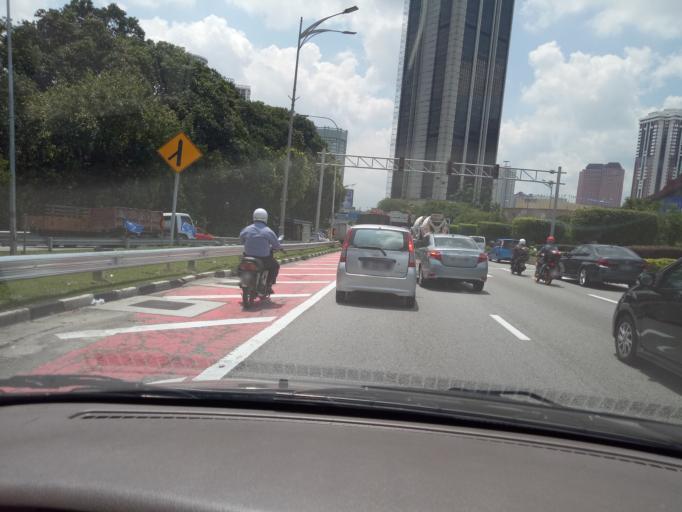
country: MY
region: Kuala Lumpur
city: Kuala Lumpur
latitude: 3.1680
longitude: 101.6886
